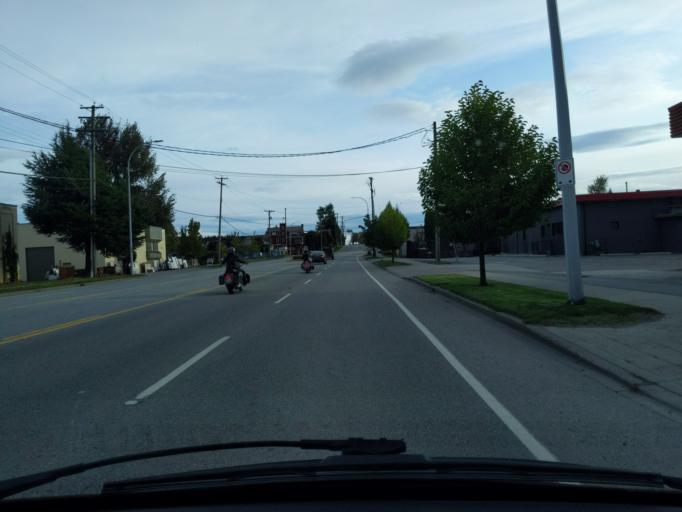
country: CA
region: British Columbia
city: Pitt Meadows
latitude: 49.1786
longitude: -122.6905
